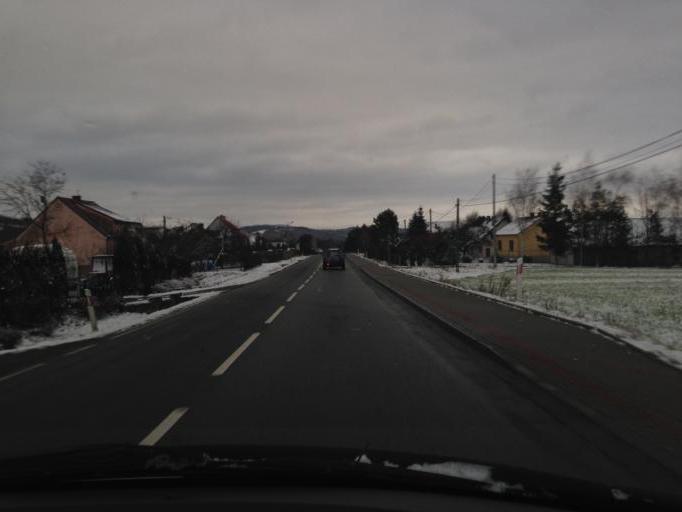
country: PL
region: Lesser Poland Voivodeship
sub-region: Powiat tarnowski
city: Gromnik
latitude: 49.8424
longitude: 20.9443
